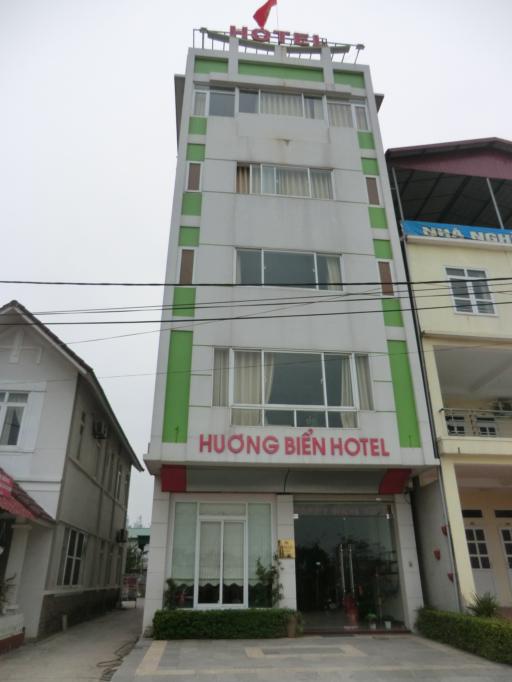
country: VN
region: Quang Ninh
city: Thanh Pho Ha Long
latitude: 20.9238
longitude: 106.9895
